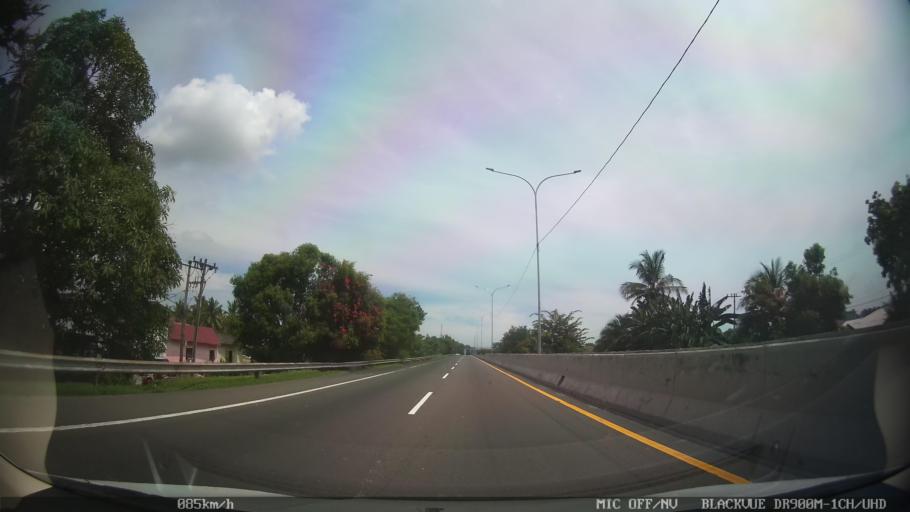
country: ID
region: North Sumatra
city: Belawan
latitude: 3.7588
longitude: 98.6828
